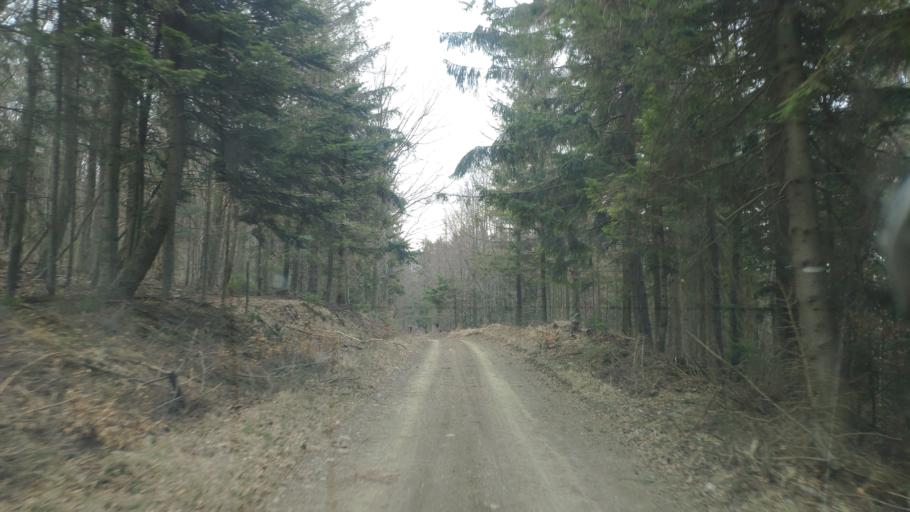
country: SK
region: Kosicky
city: Gelnica
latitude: 48.7550
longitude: 21.0400
